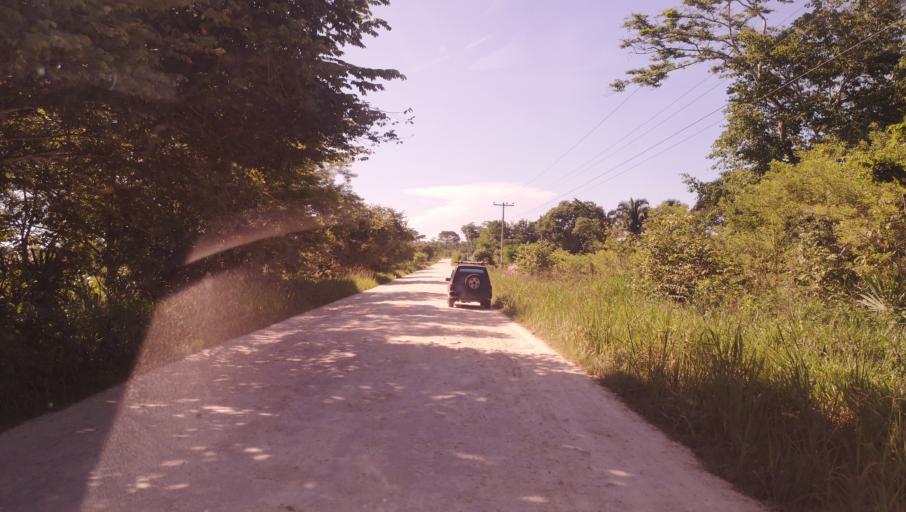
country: GT
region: Peten
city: Dolores
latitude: 16.7178
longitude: -89.3702
